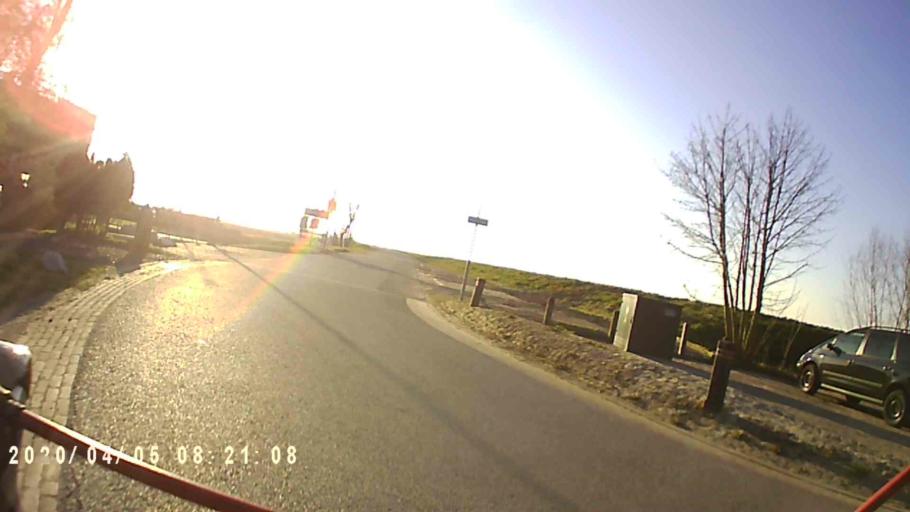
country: NL
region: Groningen
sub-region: Gemeente Zuidhorn
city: Oldehove
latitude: 53.3324
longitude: 6.4507
